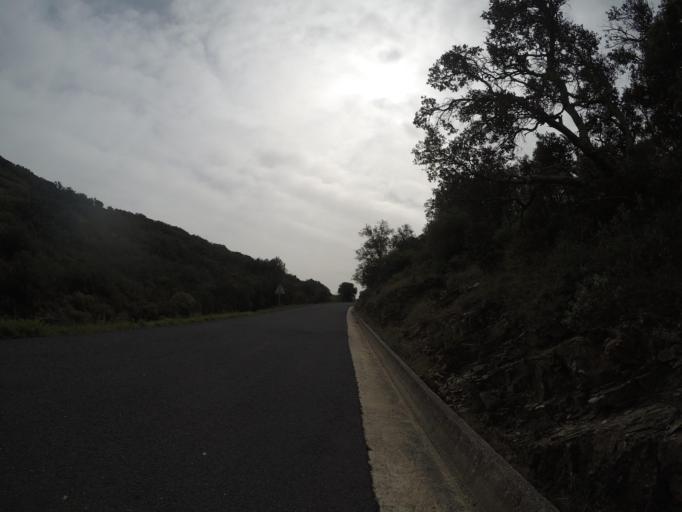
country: FR
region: Languedoc-Roussillon
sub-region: Departement des Pyrenees-Orientales
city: Estagel
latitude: 42.7427
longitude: 2.7269
